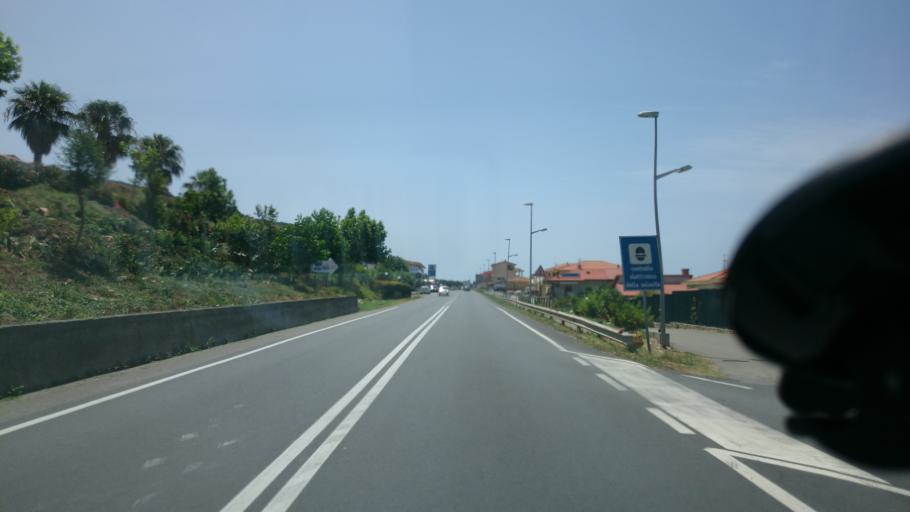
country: IT
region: Calabria
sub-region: Provincia di Cosenza
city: Cittadella del Capo
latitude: 39.5721
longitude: 15.8720
